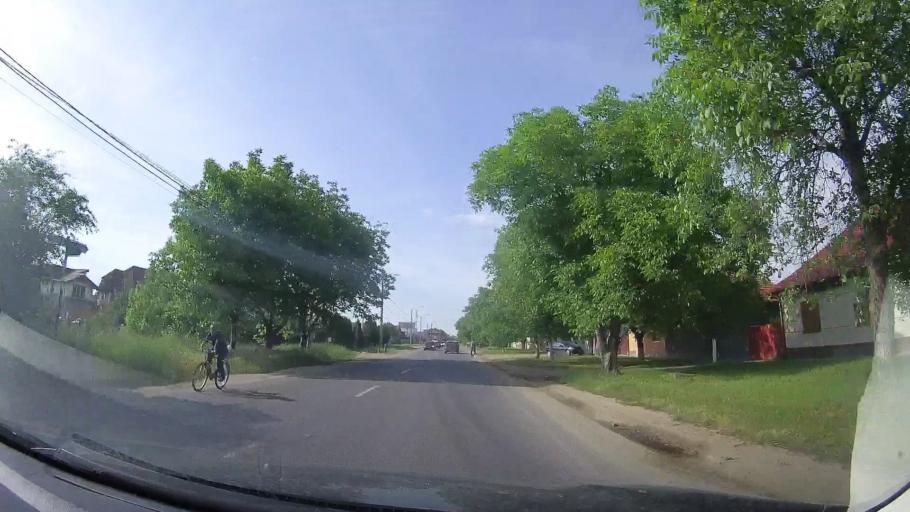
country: RO
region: Caras-Severin
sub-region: Municipiul Caransebes
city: Caransebes
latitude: 45.3912
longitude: 22.2278
